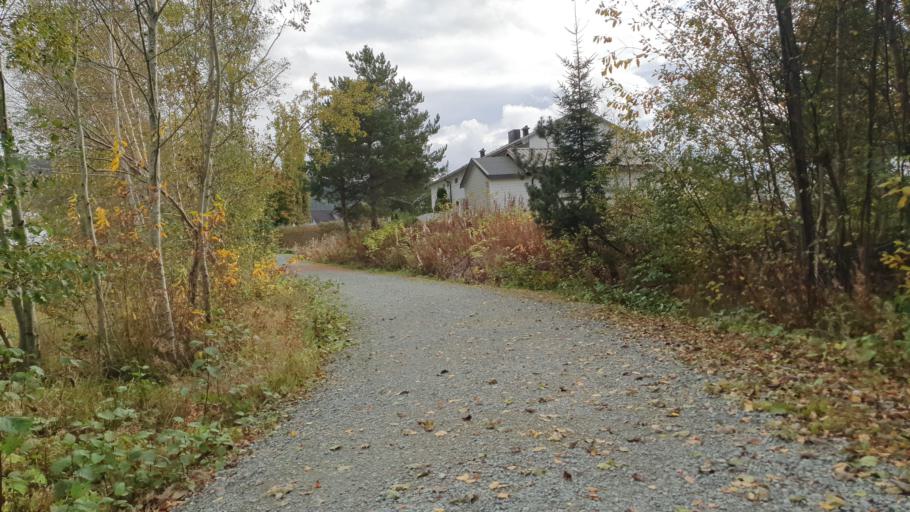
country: NO
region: Sor-Trondelag
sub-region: Klaebu
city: Klaebu
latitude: 63.3052
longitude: 10.4749
